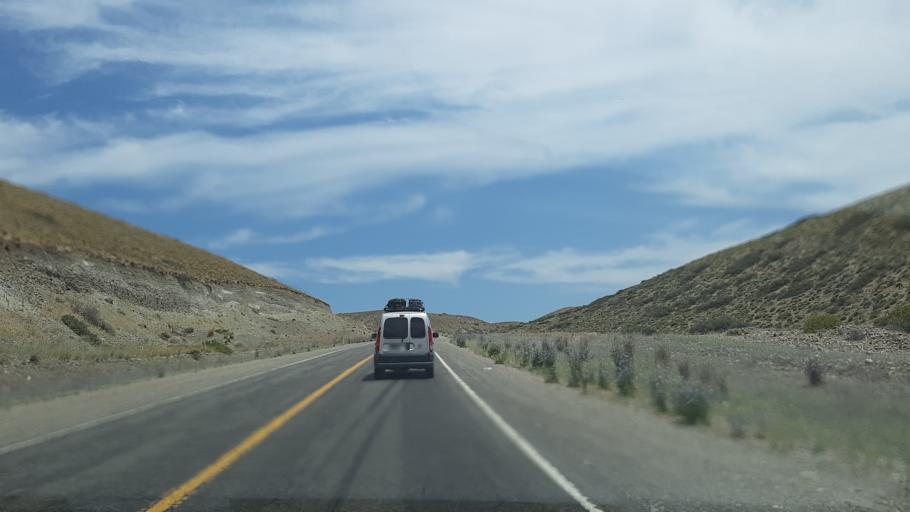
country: AR
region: Rio Negro
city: Pilcaniyeu
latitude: -40.4824
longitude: -70.6748
